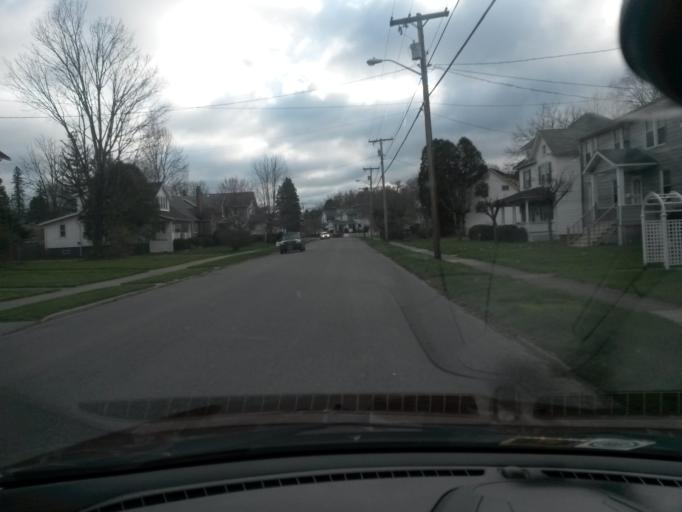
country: US
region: West Virginia
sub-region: Mercer County
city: Bluefield
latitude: 37.2536
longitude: -81.2238
